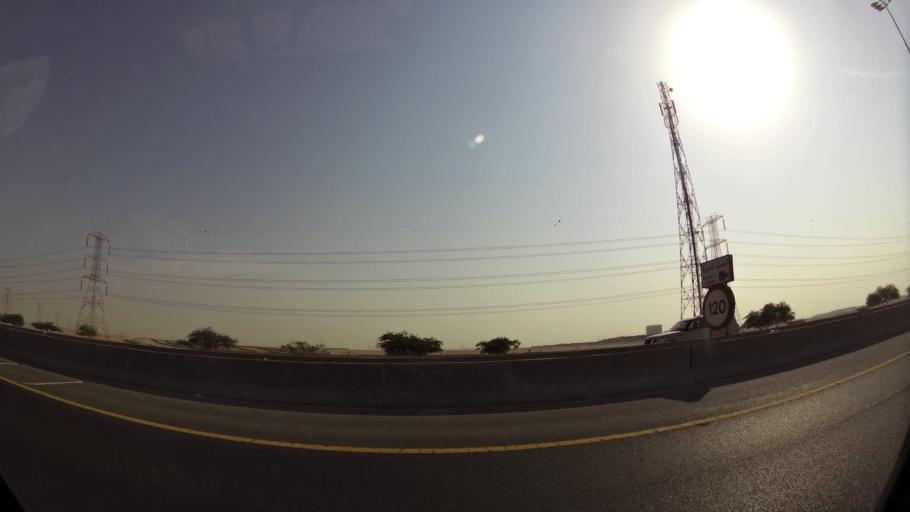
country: KW
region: Al Ahmadi
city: Al Ahmadi
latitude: 29.0211
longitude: 48.0919
